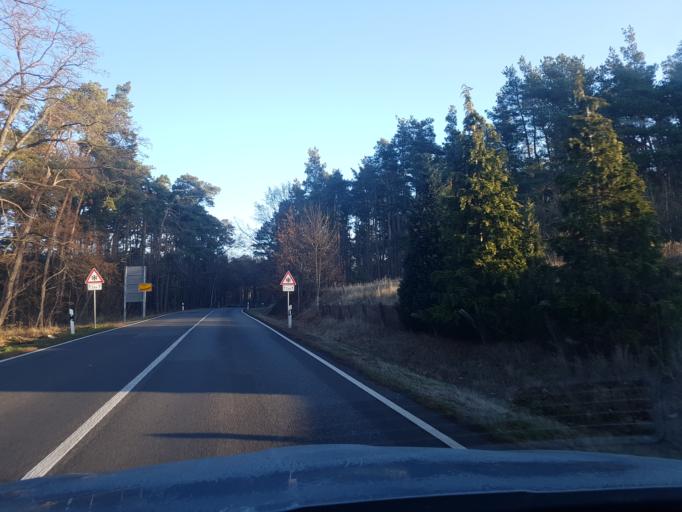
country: DE
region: Brandenburg
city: Hohenbucko
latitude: 51.7434
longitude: 13.4405
